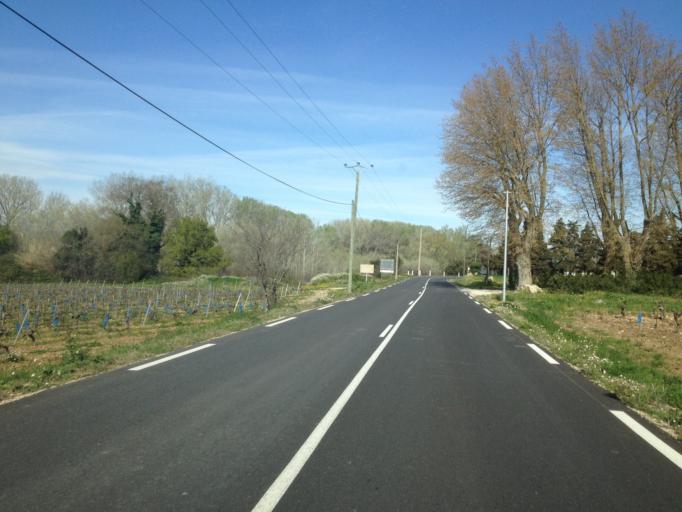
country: FR
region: Languedoc-Roussillon
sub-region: Departement du Gard
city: Roquemaure
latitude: 44.0614
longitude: 4.7987
